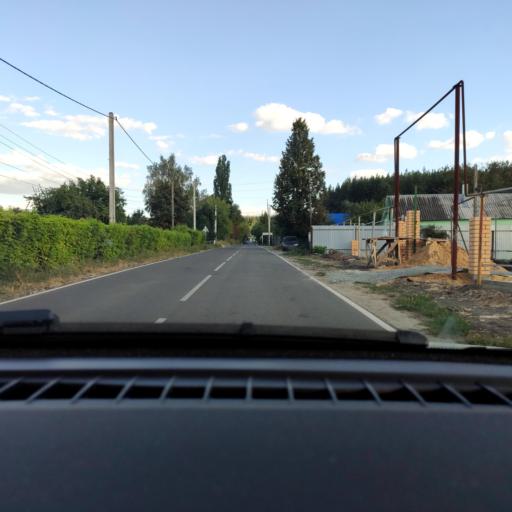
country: RU
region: Voronezj
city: Devitsa
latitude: 51.6576
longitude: 38.9757
